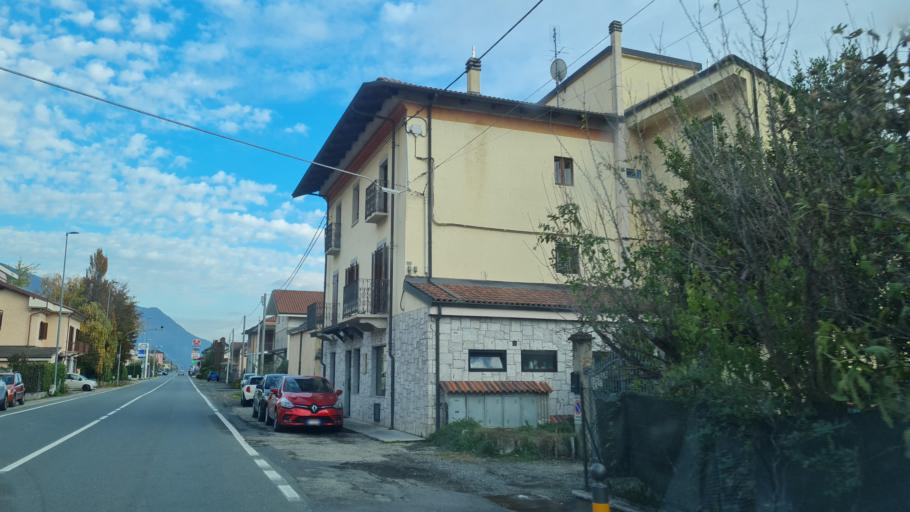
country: IT
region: Piedmont
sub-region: Provincia di Torino
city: Bussoleno
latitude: 45.1381
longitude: 7.1558
